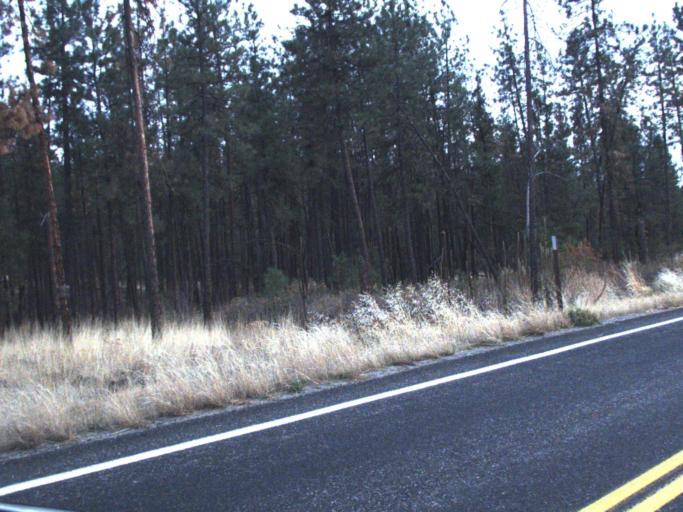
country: US
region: Washington
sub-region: Lincoln County
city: Davenport
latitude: 48.0978
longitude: -118.2013
